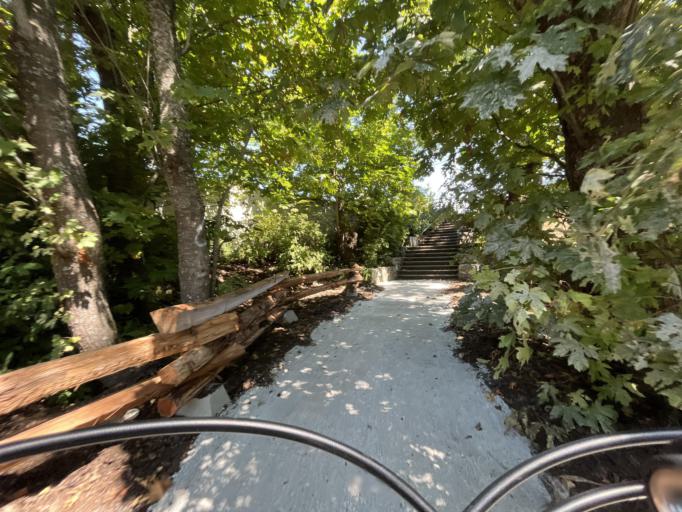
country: CA
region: British Columbia
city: Victoria
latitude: 48.4459
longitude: -123.3780
